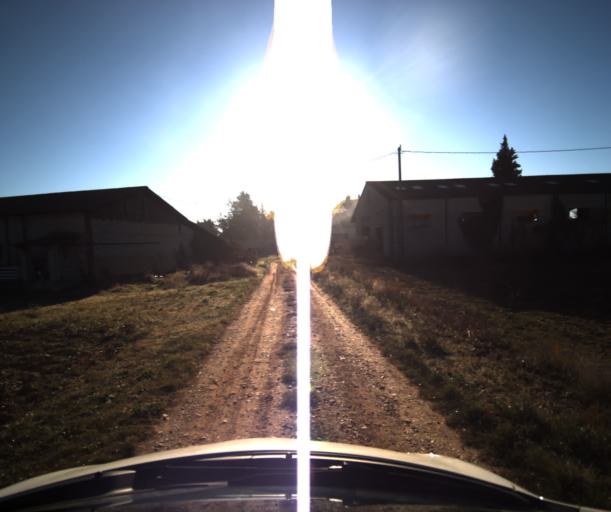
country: FR
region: Provence-Alpes-Cote d'Azur
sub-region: Departement du Vaucluse
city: Pertuis
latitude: 43.7203
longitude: 5.4910
